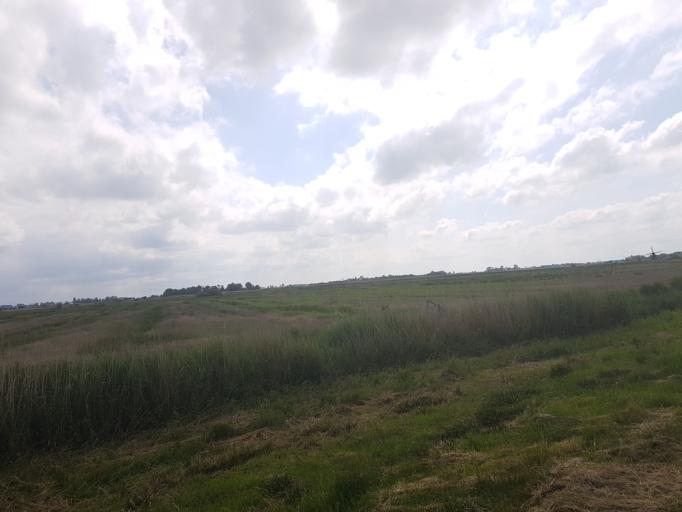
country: NL
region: Friesland
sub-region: Gemeente Boarnsterhim
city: Aldeboarn
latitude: 53.0974
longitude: 5.9025
